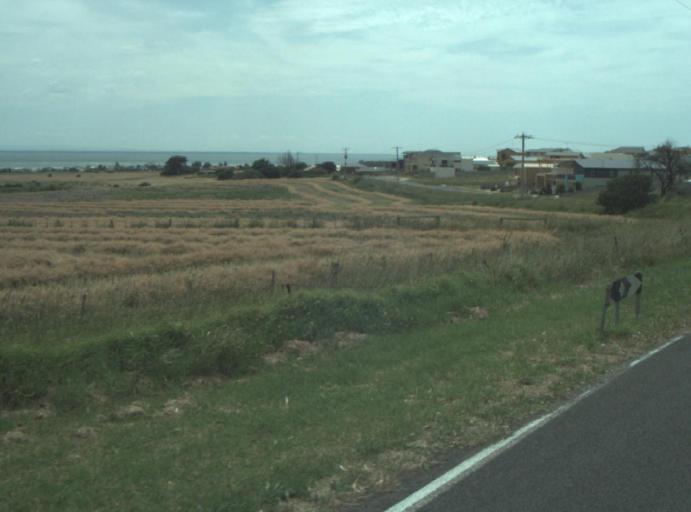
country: AU
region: Victoria
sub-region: Greater Geelong
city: Clifton Springs
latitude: -38.1281
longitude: 144.6258
